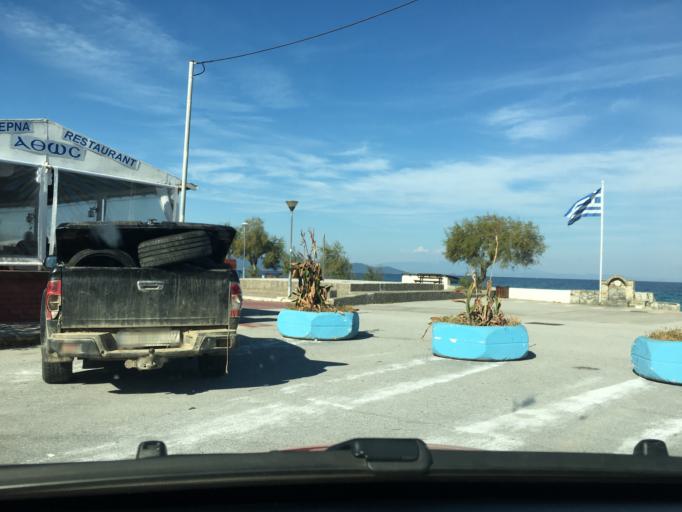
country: GR
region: Central Macedonia
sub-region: Nomos Chalkidikis
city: Ierissos
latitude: 40.4002
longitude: 23.8810
